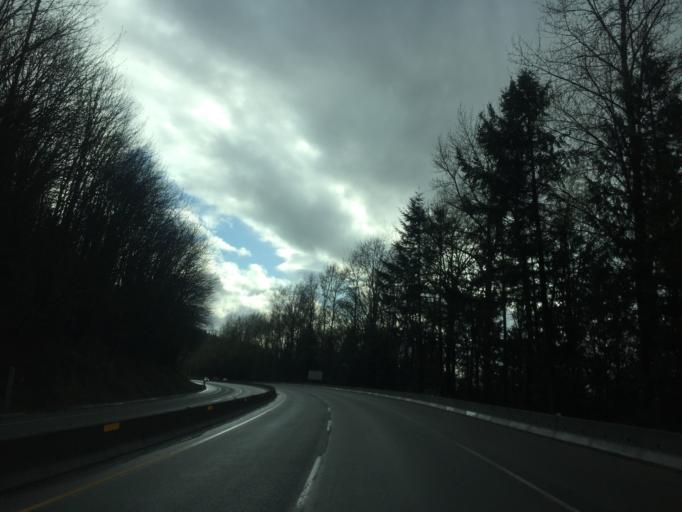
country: CA
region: British Columbia
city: Agassiz
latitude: 49.1716
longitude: -121.7809
